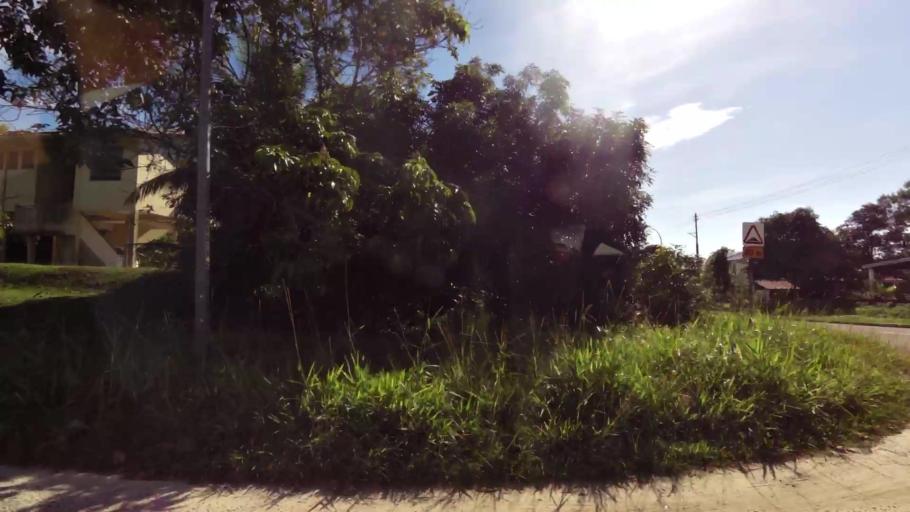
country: BN
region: Brunei and Muara
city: Bandar Seri Begawan
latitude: 4.9767
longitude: 114.9597
